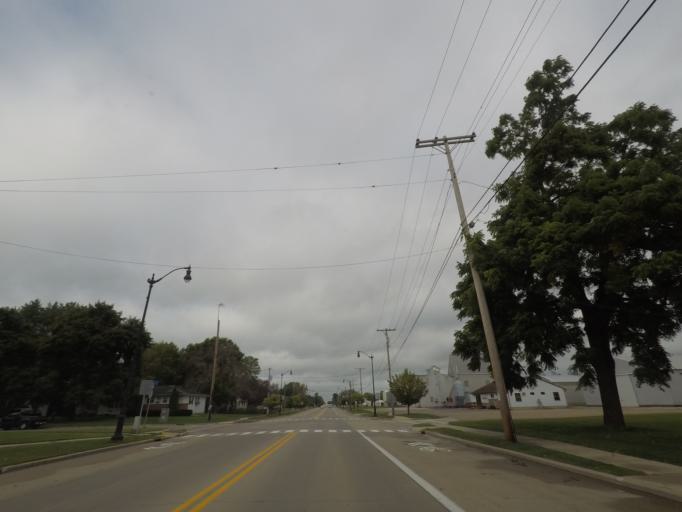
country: US
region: Wisconsin
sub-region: Jefferson County
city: Jefferson
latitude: 43.0058
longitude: -88.8211
